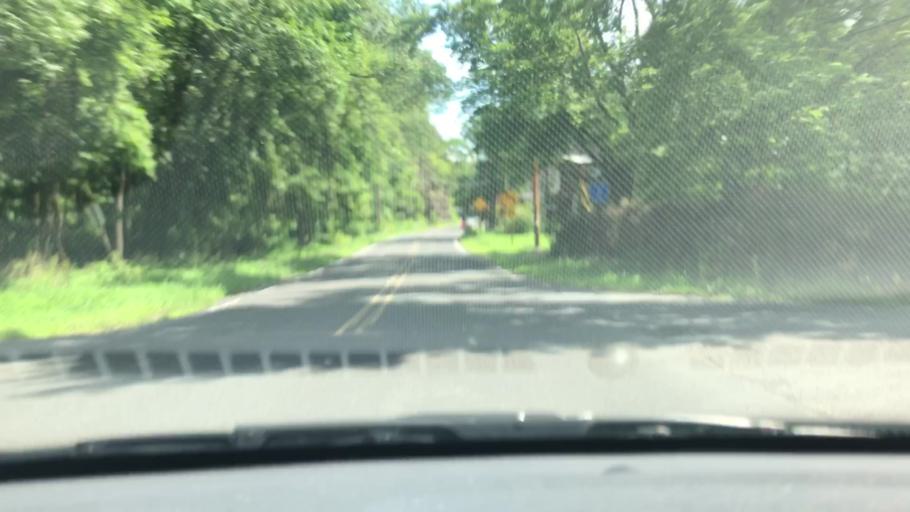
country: US
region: New York
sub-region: Ulster County
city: Stone Ridge
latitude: 41.8869
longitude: -74.1243
